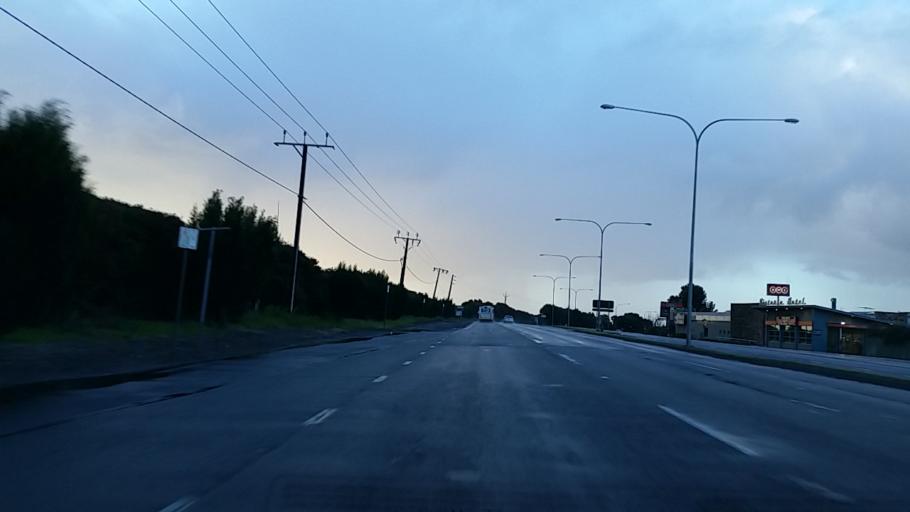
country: AU
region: South Australia
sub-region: Onkaparinga
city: Bedford Park
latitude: -35.0517
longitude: 138.5593
